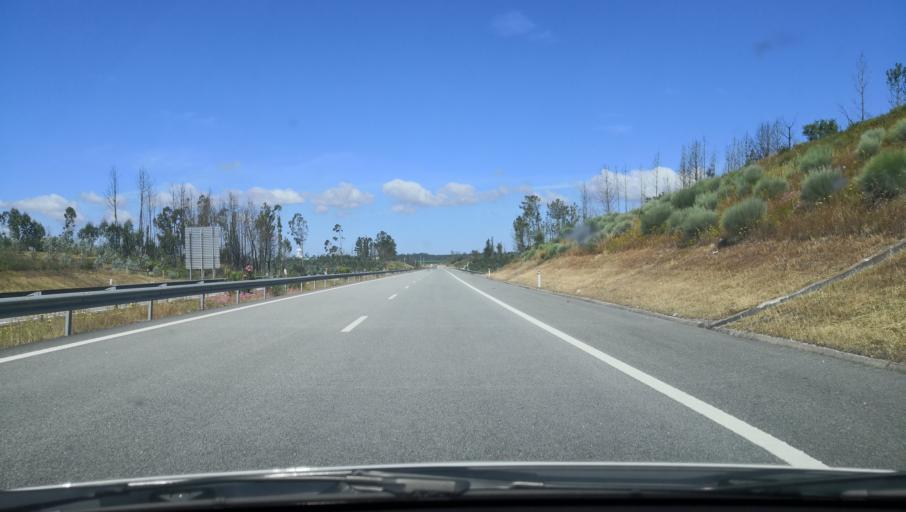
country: PT
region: Coimbra
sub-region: Cantanhede
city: Cantanhede
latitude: 40.2842
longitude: -8.5525
